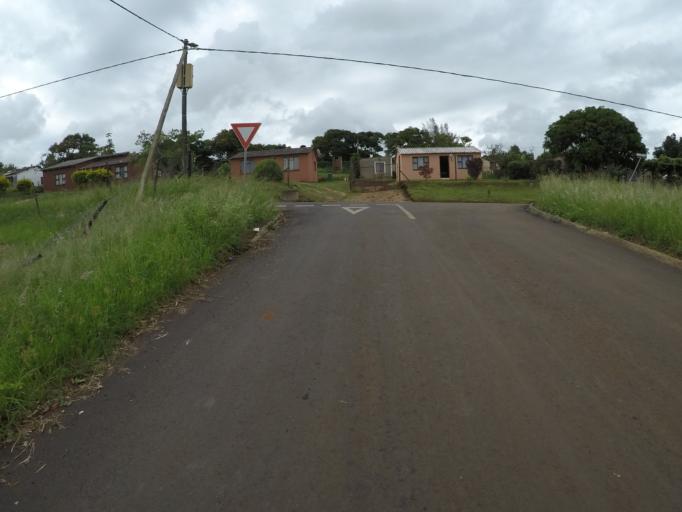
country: ZA
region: KwaZulu-Natal
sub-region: uThungulu District Municipality
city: Empangeni
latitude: -28.7698
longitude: 31.8706
